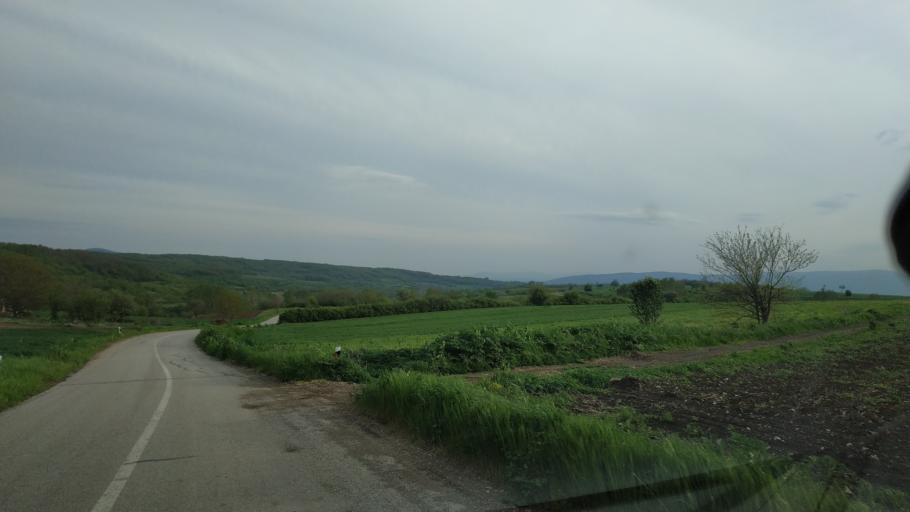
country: RS
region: Central Serbia
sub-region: Zajecarski Okrug
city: Soko Banja
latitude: 43.5242
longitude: 21.8482
